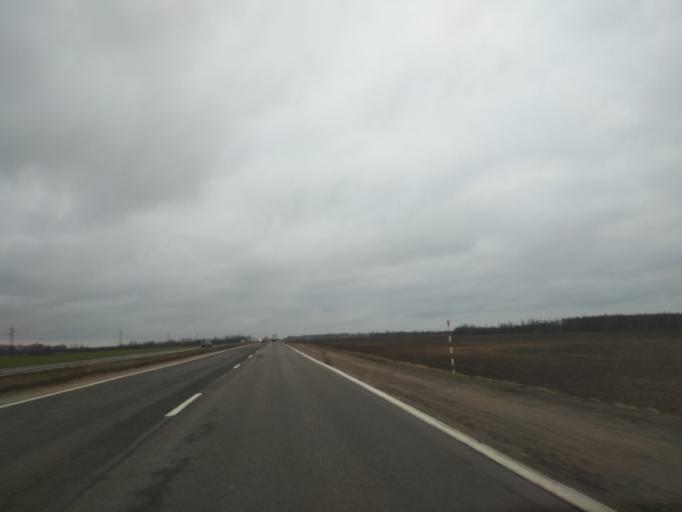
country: BY
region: Minsk
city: Dukora
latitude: 53.6502
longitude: 27.9735
